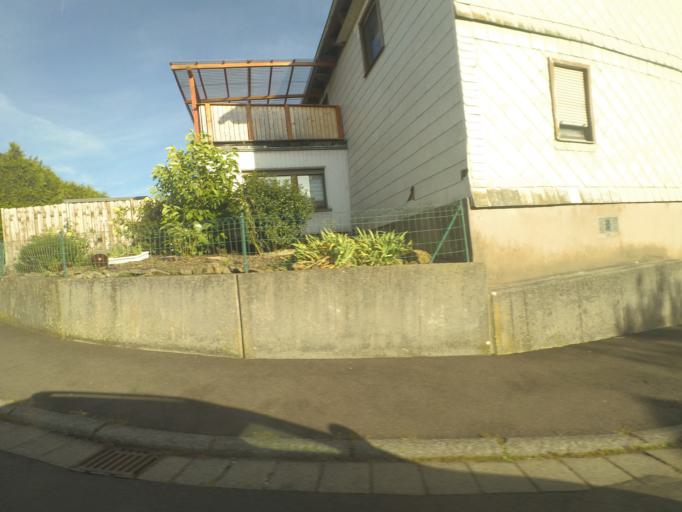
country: DE
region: Hesse
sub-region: Regierungsbezirk Giessen
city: Freiensteinau
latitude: 50.4161
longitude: 9.4661
